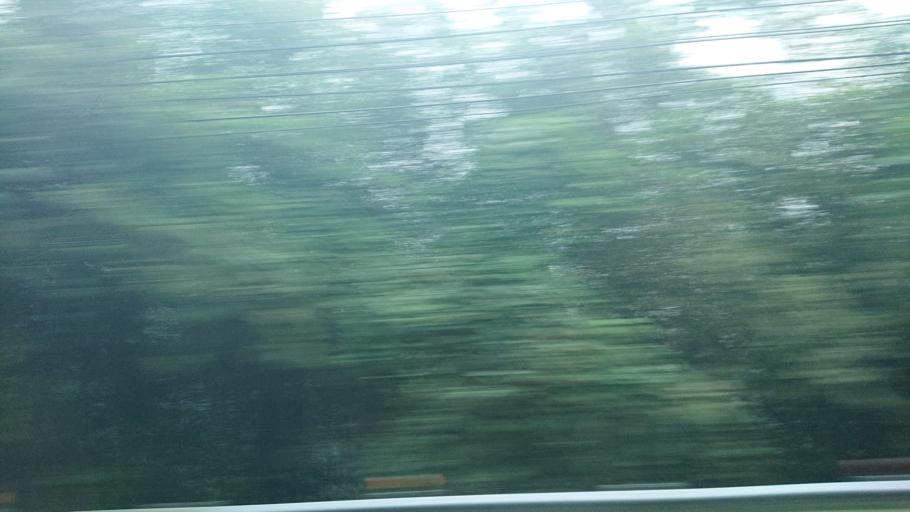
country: TW
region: Taiwan
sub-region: Chiayi
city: Jiayi Shi
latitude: 23.4773
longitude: 120.7138
